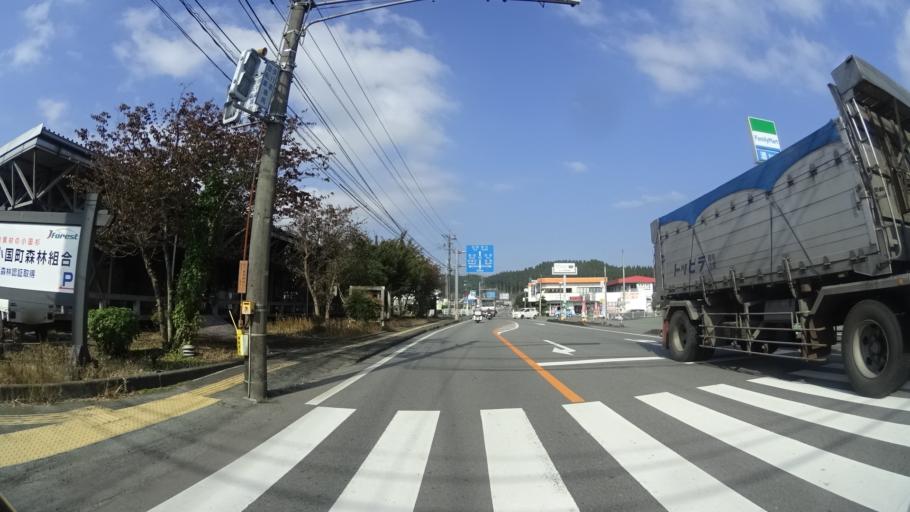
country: JP
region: Oita
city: Tsukawaki
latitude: 33.1219
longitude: 131.0613
